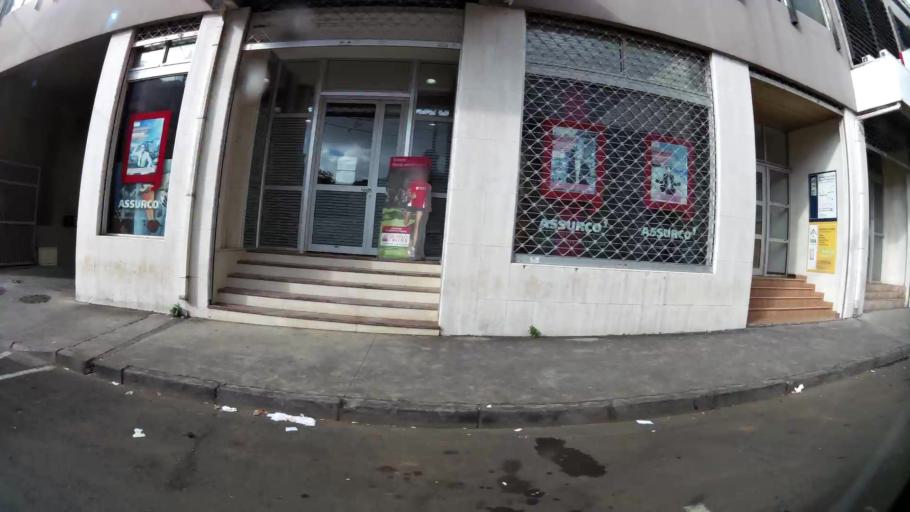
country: RE
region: Reunion
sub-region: Reunion
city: Saint-Denis
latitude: -20.8766
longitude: 55.4536
